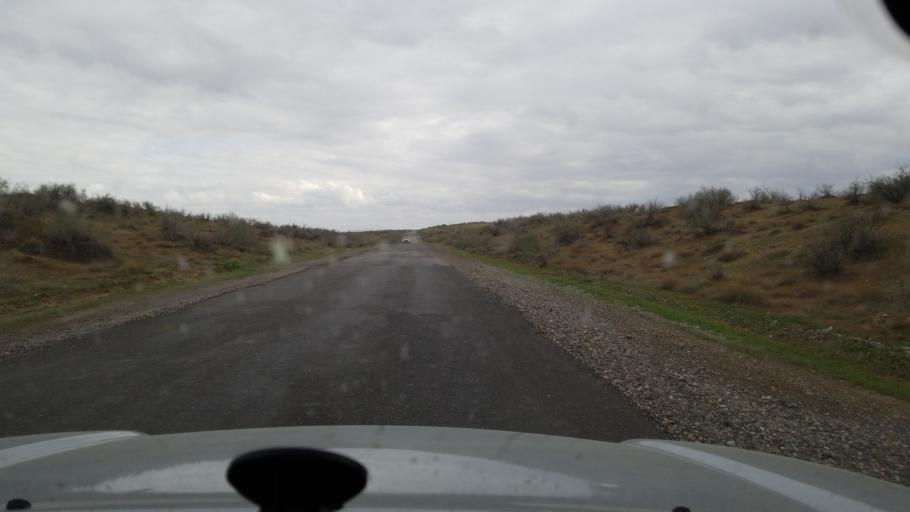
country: TM
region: Mary
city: Serhetabat
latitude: 36.0874
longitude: 62.6129
